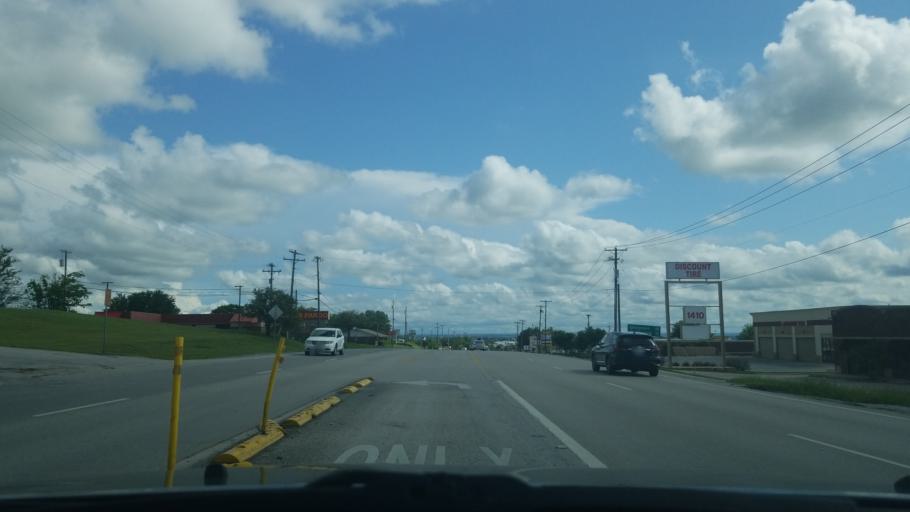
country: US
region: Texas
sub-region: Wise County
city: Decatur
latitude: 33.2253
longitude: -97.5945
